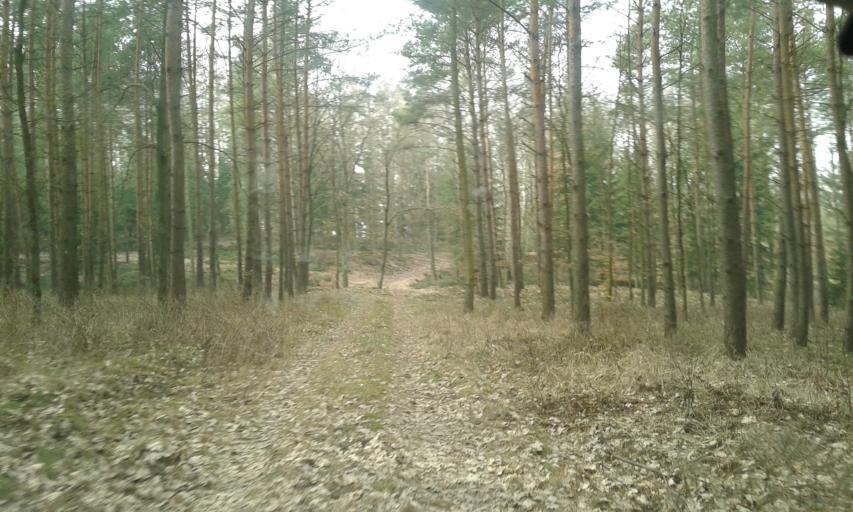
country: PL
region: West Pomeranian Voivodeship
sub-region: Powiat choszczenski
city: Pelczyce
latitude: 53.0857
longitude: 15.2326
